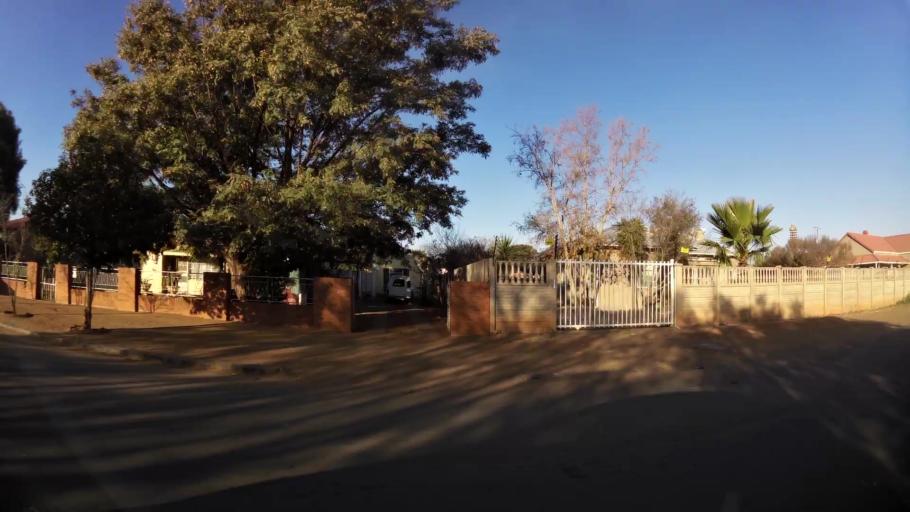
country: ZA
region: Northern Cape
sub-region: Frances Baard District Municipality
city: Kimberley
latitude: -28.7369
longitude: 24.7423
